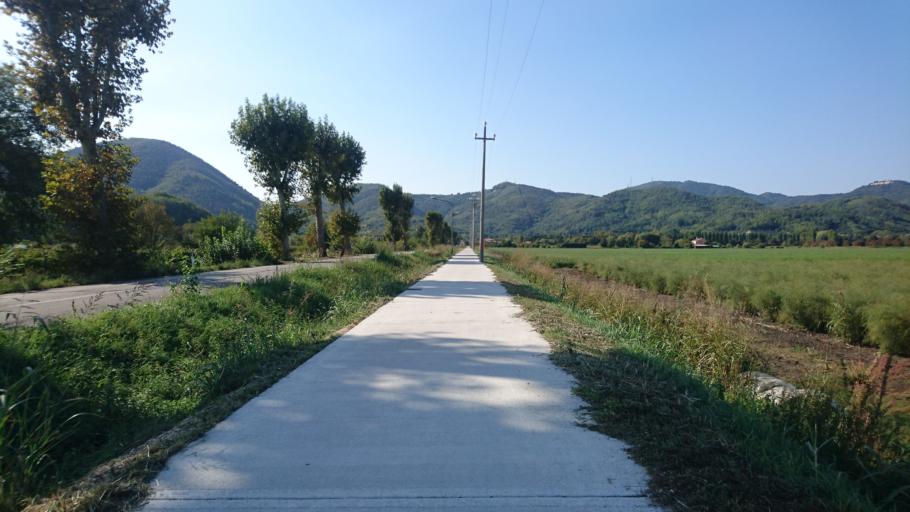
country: IT
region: Veneto
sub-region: Provincia di Padova
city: Galzignano
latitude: 45.2874
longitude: 11.7500
